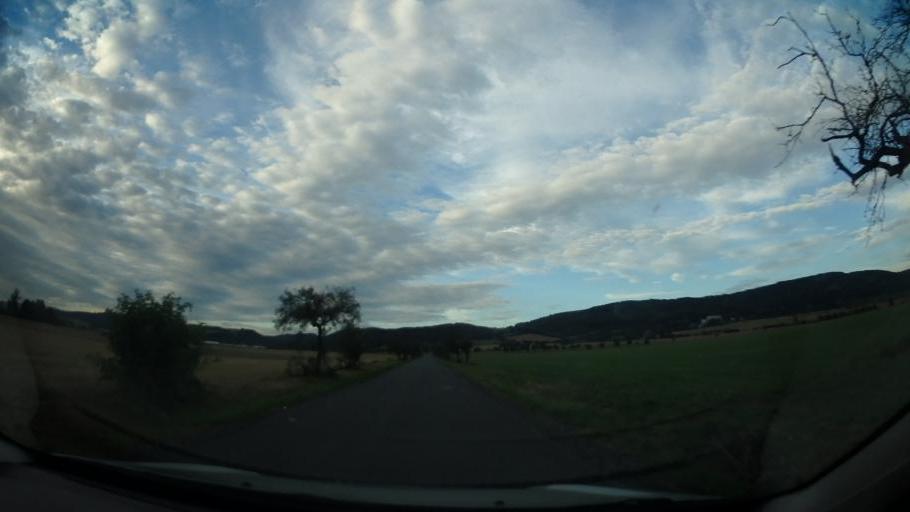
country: CZ
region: Olomoucky
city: Paseka
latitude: 49.8036
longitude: 17.1989
